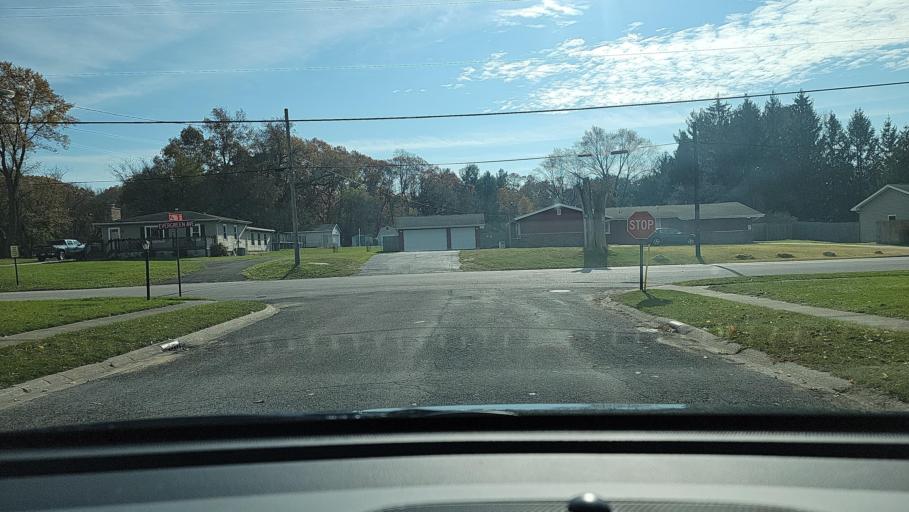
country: US
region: Indiana
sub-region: Lake County
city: Lake Station
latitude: 41.5798
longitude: -87.2107
